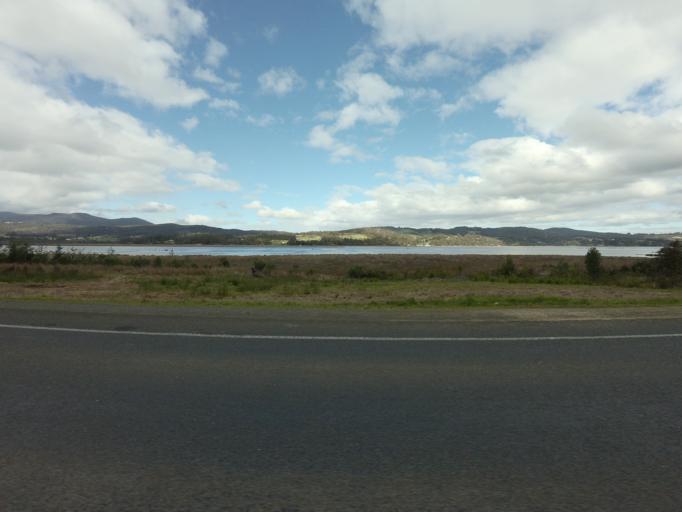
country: AU
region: Tasmania
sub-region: Huon Valley
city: Franklin
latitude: -43.1176
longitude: 146.9916
